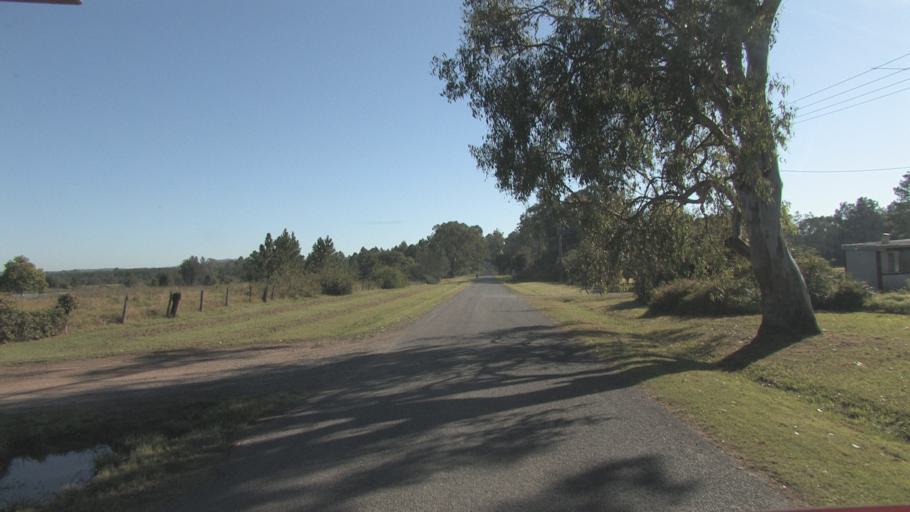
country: AU
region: Queensland
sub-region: Gold Coast
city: Yatala
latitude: -27.6894
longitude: 153.2605
